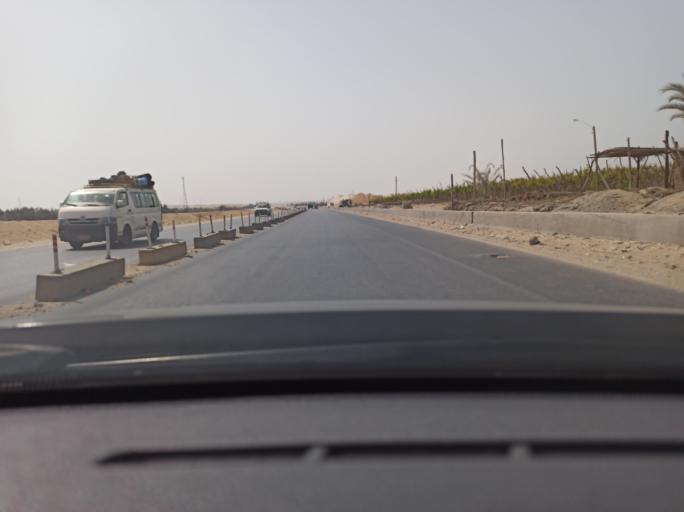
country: EG
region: Muhafazat al Fayyum
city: Al Wasitah
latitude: 29.2721
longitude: 31.2650
